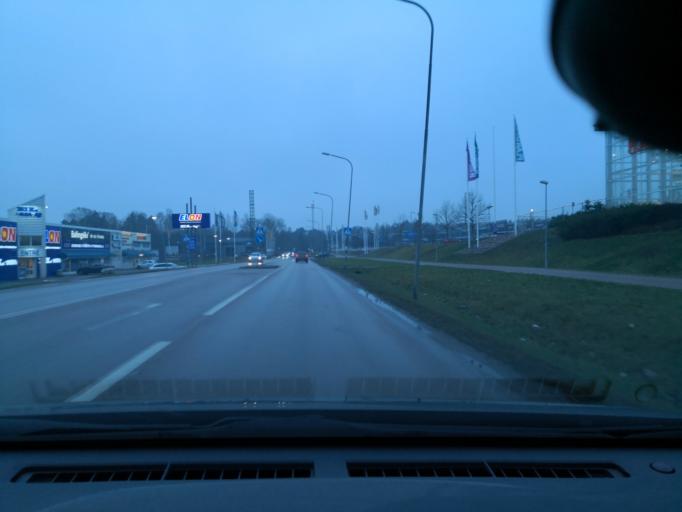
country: SE
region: Vaestmanland
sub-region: Vasteras
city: Vasteras
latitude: 59.6106
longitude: 16.6128
